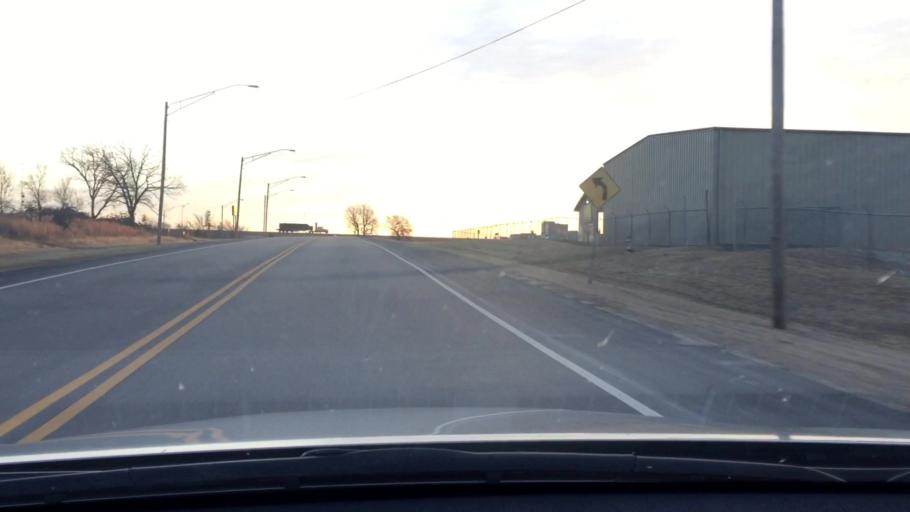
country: US
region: Oklahoma
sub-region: Carter County
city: Ardmore
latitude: 34.1749
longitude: -97.1727
